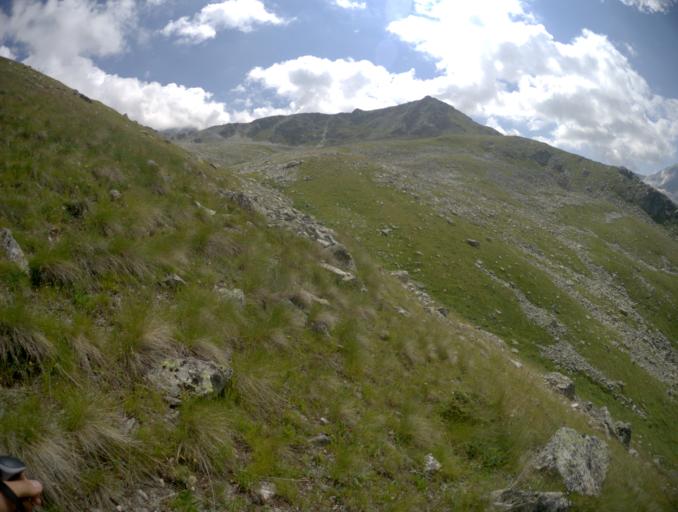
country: RU
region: Karachayevo-Cherkesiya
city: Uchkulan
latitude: 43.3009
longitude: 42.0638
